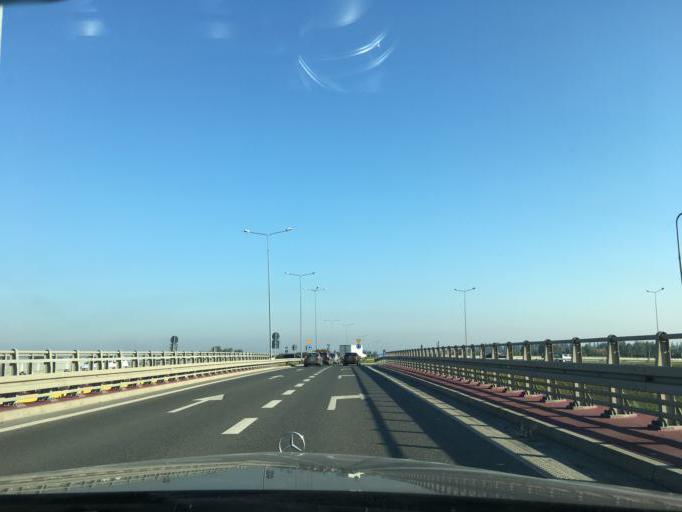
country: PL
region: Masovian Voivodeship
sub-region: Powiat grodziski
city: Grodzisk Mazowiecki
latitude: 52.1448
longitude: 20.6094
